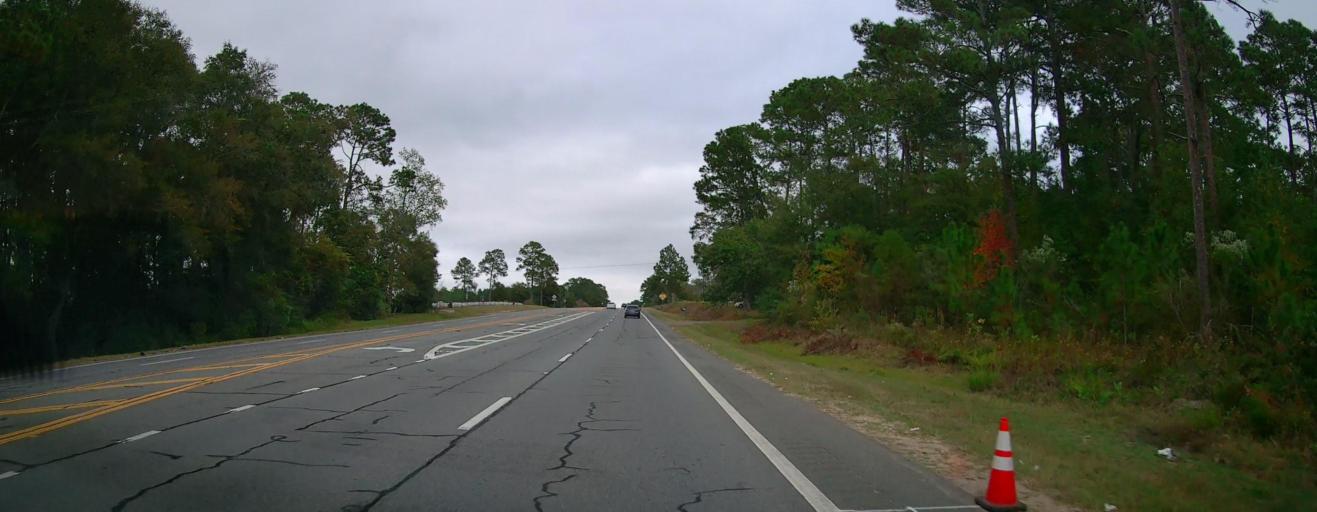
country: US
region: Georgia
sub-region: Colquitt County
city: Moultrie
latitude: 31.2598
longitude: -83.7005
